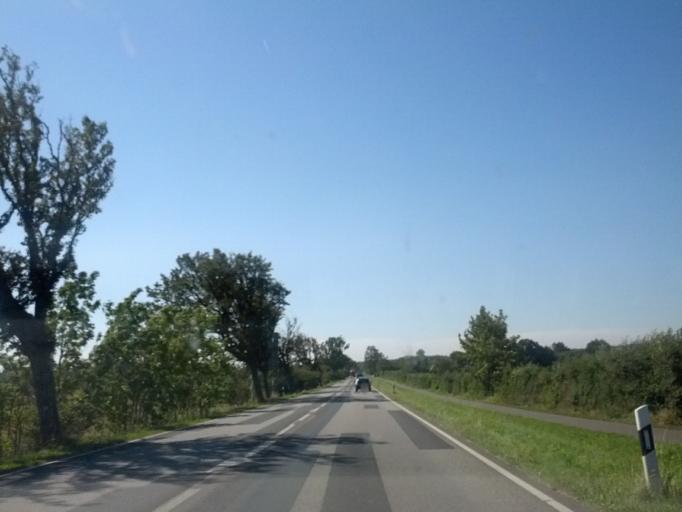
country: DE
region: Mecklenburg-Vorpommern
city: Sagard
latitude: 54.5086
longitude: 13.5339
